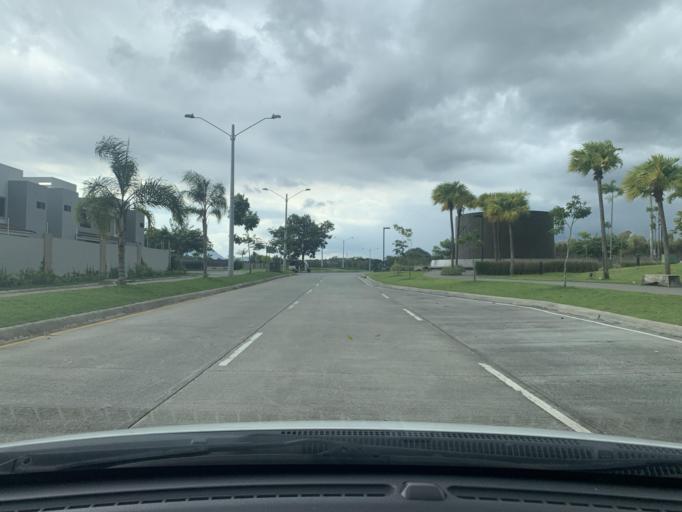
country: PA
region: Panama
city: San Miguelito
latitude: 9.0915
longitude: -79.4695
